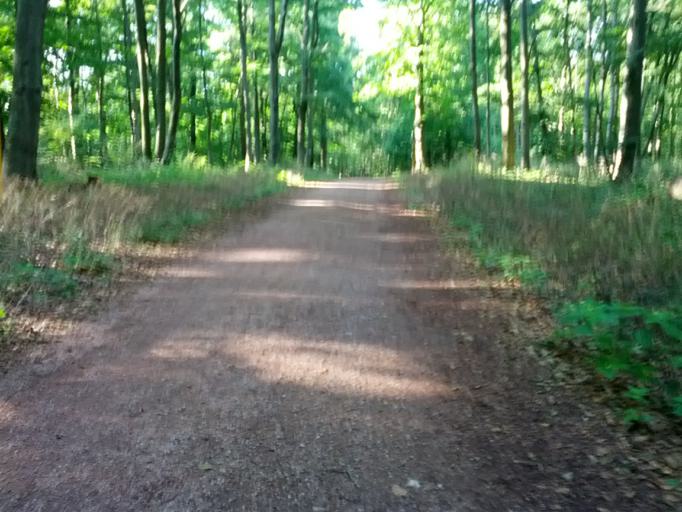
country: DE
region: Thuringia
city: Eisenach
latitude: 50.9334
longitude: 10.3143
